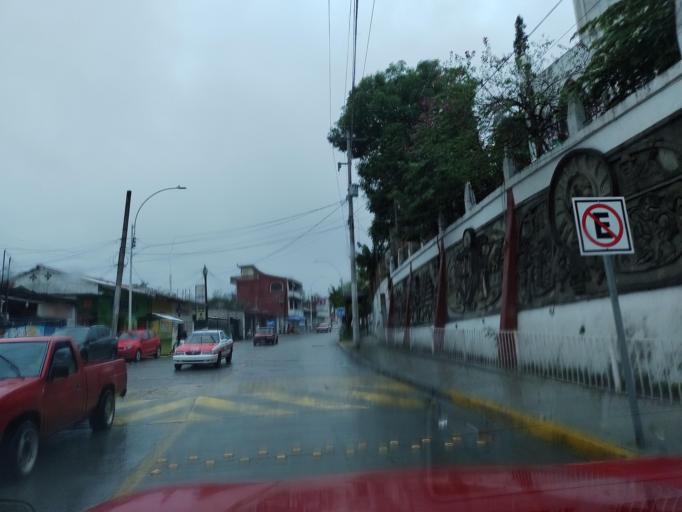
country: MX
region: Veracruz
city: Papantla de Olarte
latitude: 20.4497
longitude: -97.3285
